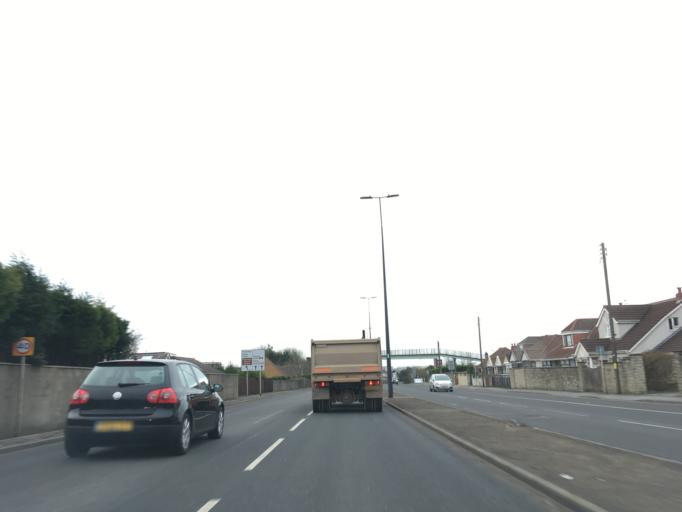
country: GB
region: England
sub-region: South Gloucestershire
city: Almondsbury
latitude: 51.5380
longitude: -2.5666
